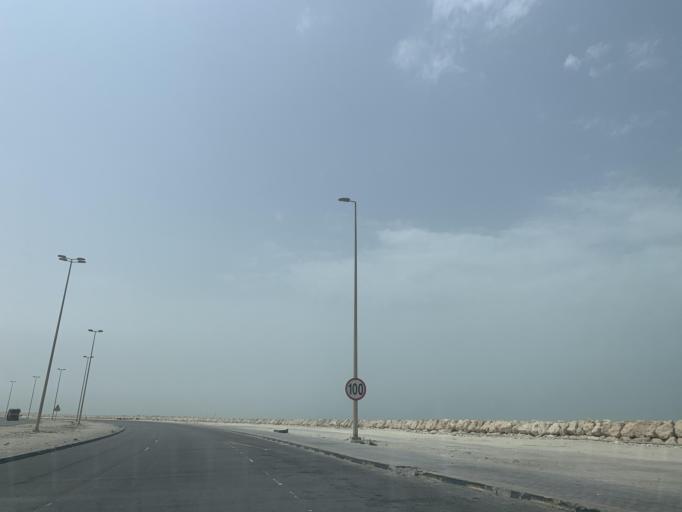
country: BH
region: Muharraq
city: Al Hadd
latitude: 26.2249
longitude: 50.6952
